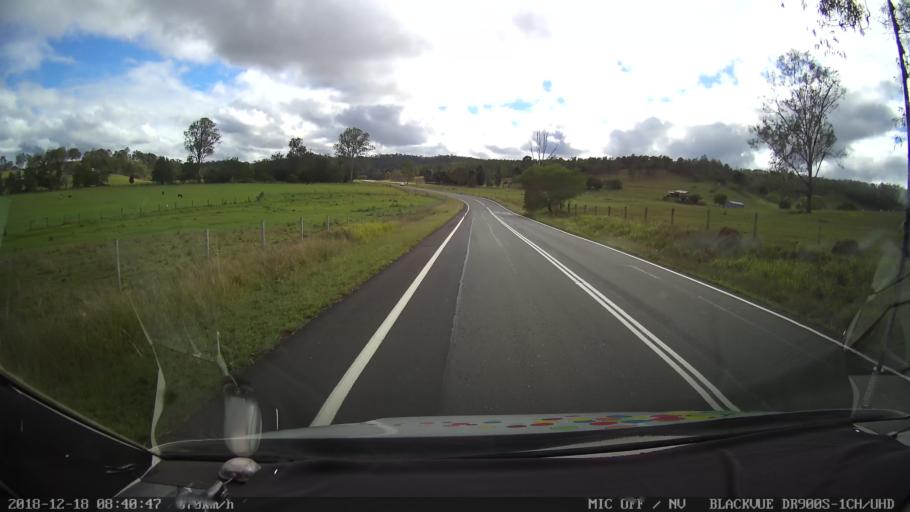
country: AU
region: Queensland
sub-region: Logan
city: Cedar Vale
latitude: -28.2408
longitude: 152.8507
